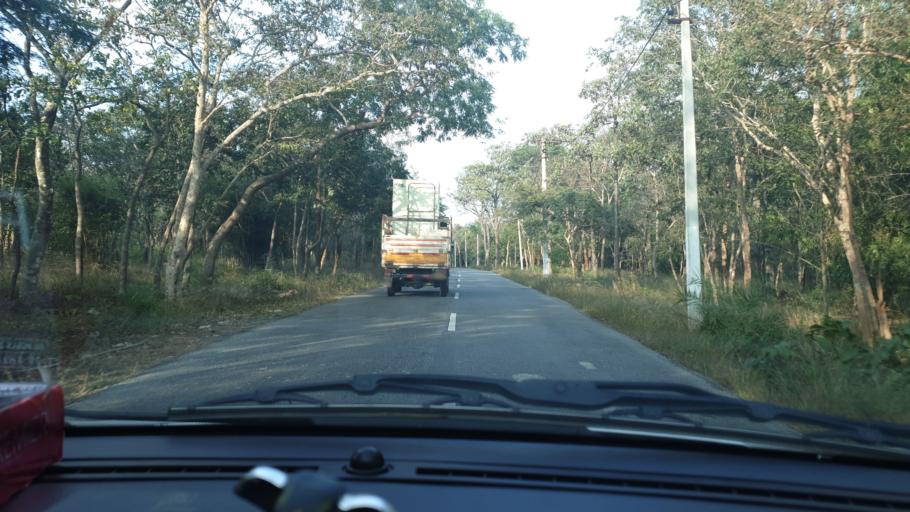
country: IN
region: Andhra Pradesh
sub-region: Kurnool
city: Srisailam
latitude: 16.2904
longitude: 78.7299
